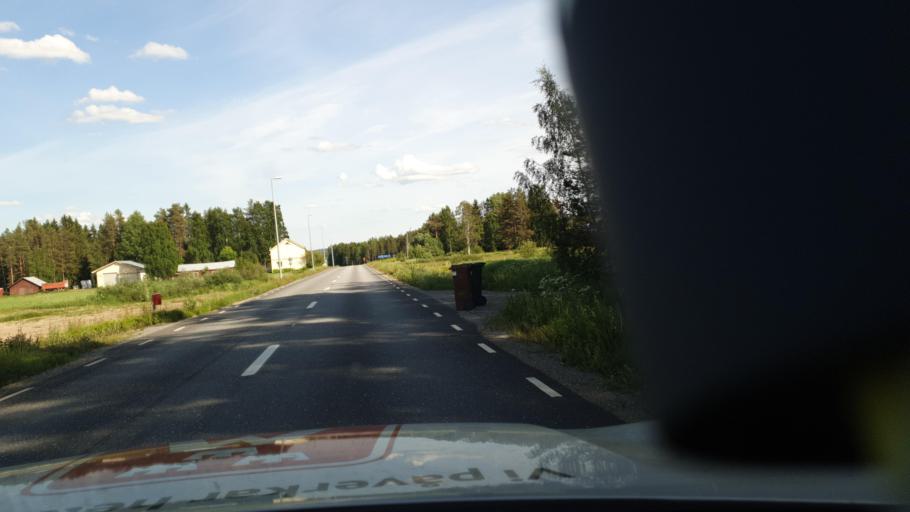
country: SE
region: Vaesterbotten
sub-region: Skelleftea Kommun
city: Forsbacka
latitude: 64.6872
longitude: 20.5208
